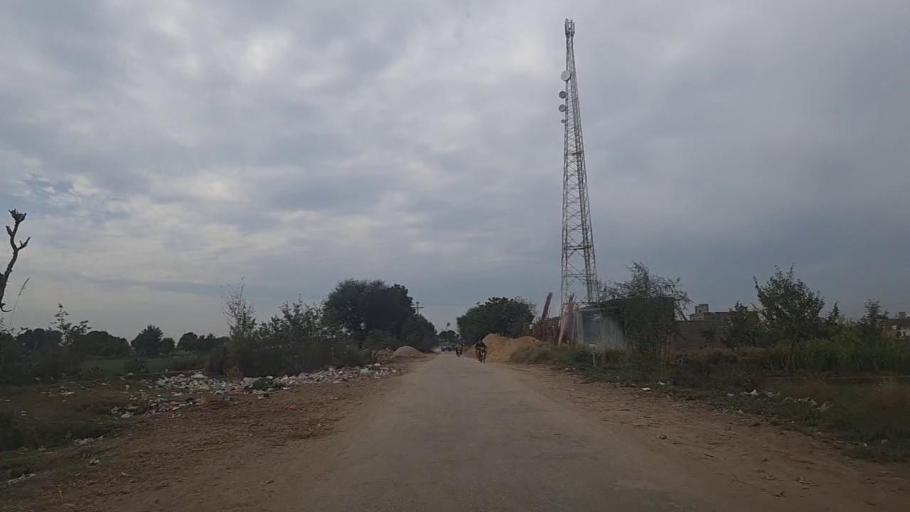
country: PK
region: Sindh
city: Khadro
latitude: 26.1287
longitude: 68.8039
